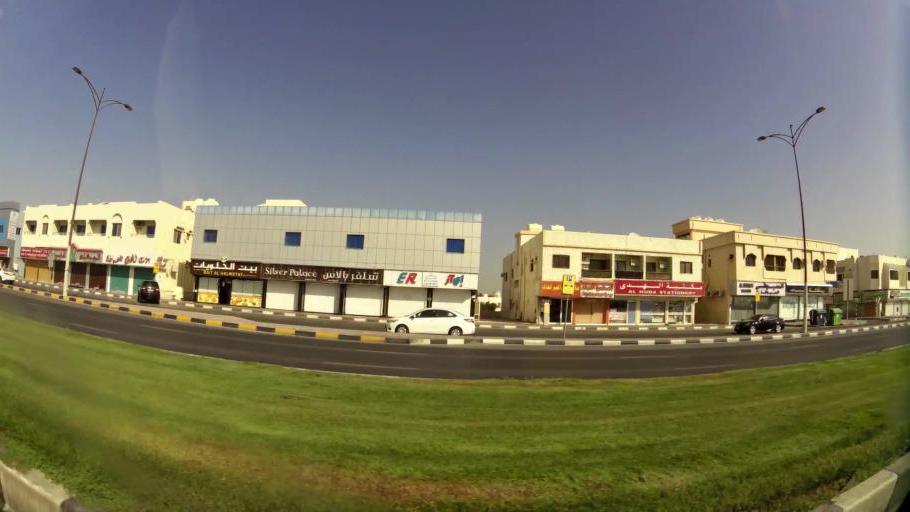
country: AE
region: Ash Shariqah
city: Sharjah
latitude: 25.3433
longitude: 55.4306
